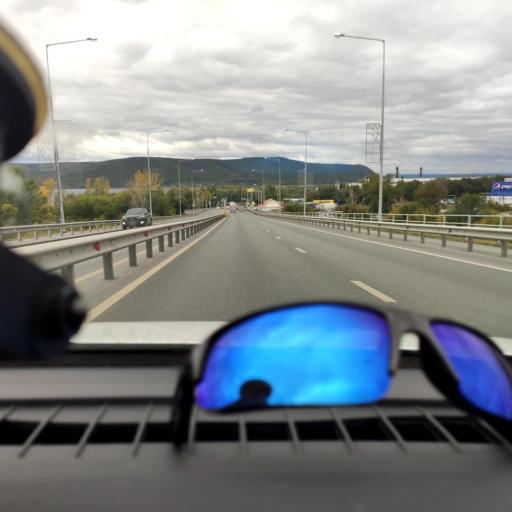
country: RU
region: Samara
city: Volzhskiy
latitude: 53.3709
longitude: 50.1840
